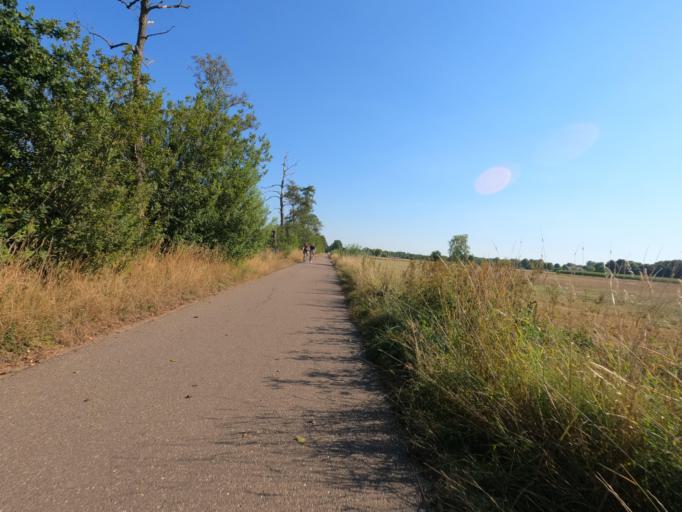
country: NL
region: Limburg
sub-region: Gemeente Roerdalen
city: Vlodrop
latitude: 51.1421
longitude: 6.0932
